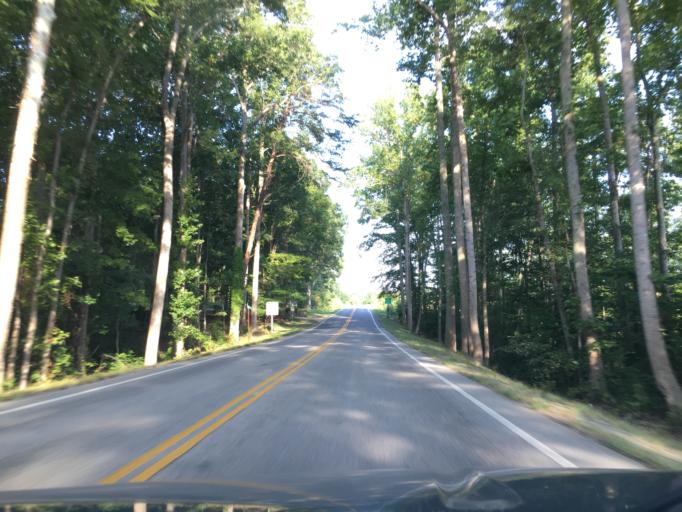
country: US
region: Virginia
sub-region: Franklin County
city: Union Hall
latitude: 36.9753
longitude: -79.6133
